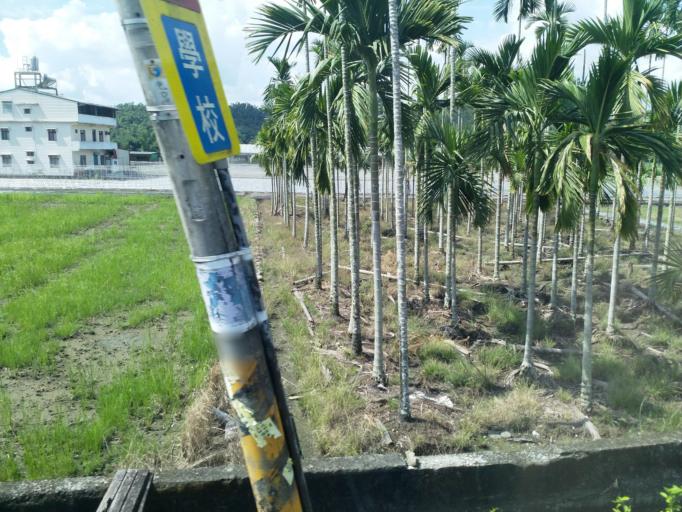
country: TW
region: Taiwan
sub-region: Pingtung
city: Pingtung
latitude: 22.8861
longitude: 120.5787
